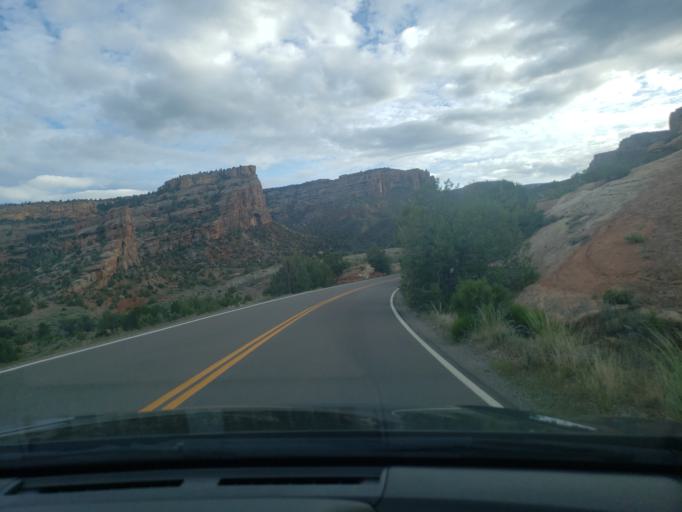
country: US
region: Colorado
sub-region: Mesa County
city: Redlands
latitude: 39.0299
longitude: -108.6310
